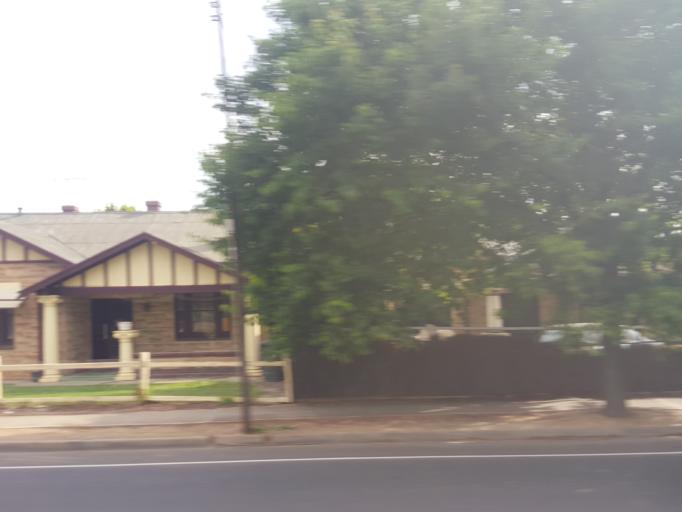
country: AU
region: South Australia
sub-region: Charles Sturt
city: Allenby Gardens
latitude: -34.8895
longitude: 138.5719
